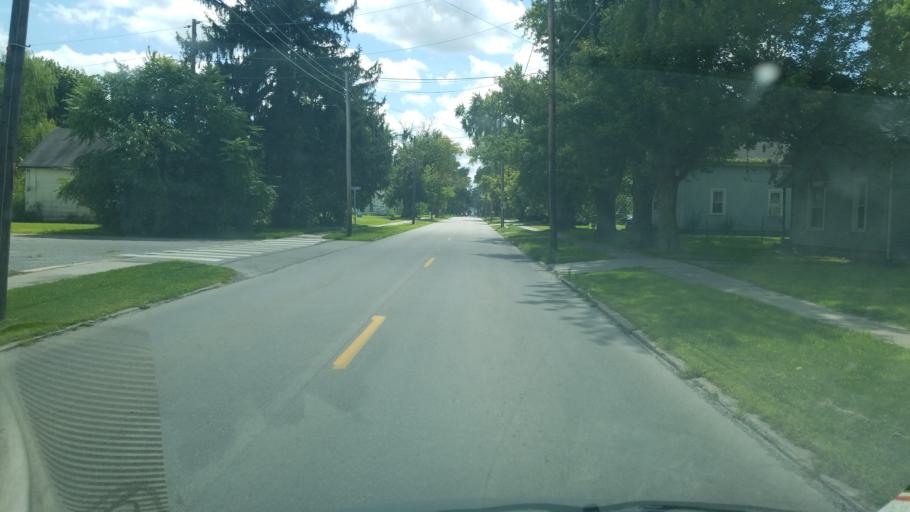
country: US
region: Ohio
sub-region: Henry County
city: Liberty Center
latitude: 41.4501
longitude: -84.0088
